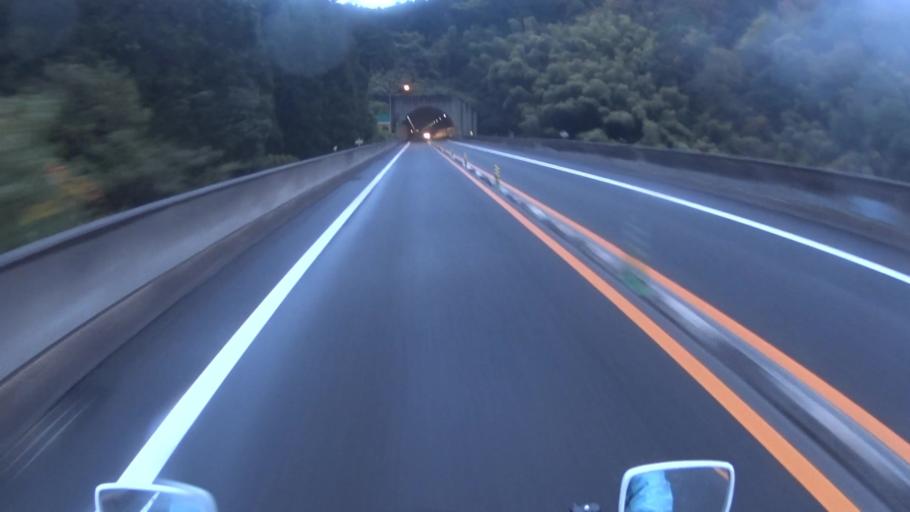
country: JP
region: Kyoto
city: Ayabe
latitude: 35.4074
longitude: 135.2276
